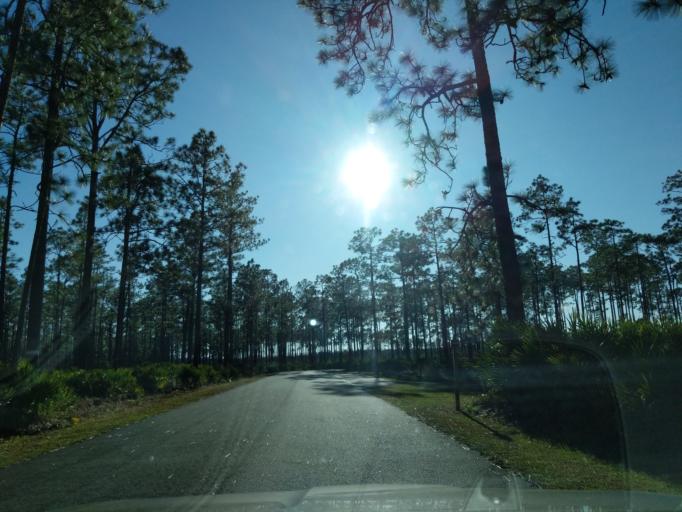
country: US
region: Georgia
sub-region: Charlton County
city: Folkston
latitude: 30.7293
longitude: -82.1371
